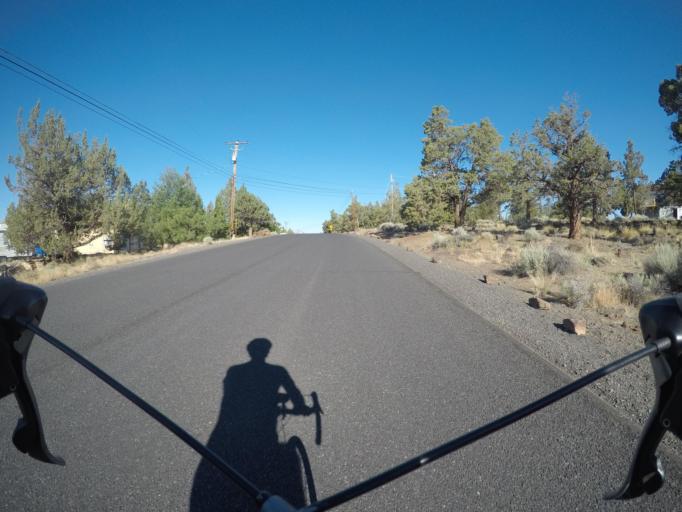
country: US
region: Oregon
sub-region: Deschutes County
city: Bend
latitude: 44.1731
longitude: -121.2749
